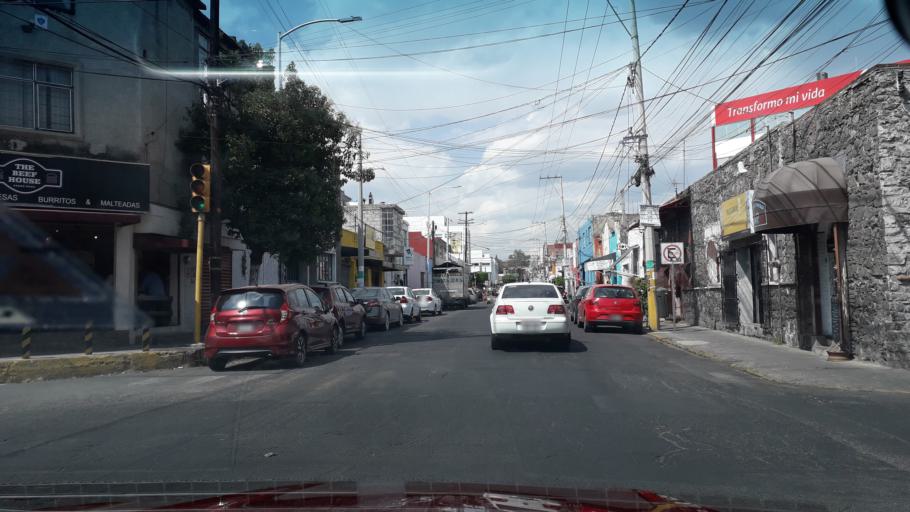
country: MX
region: Puebla
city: Puebla
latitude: 19.0467
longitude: -98.2167
